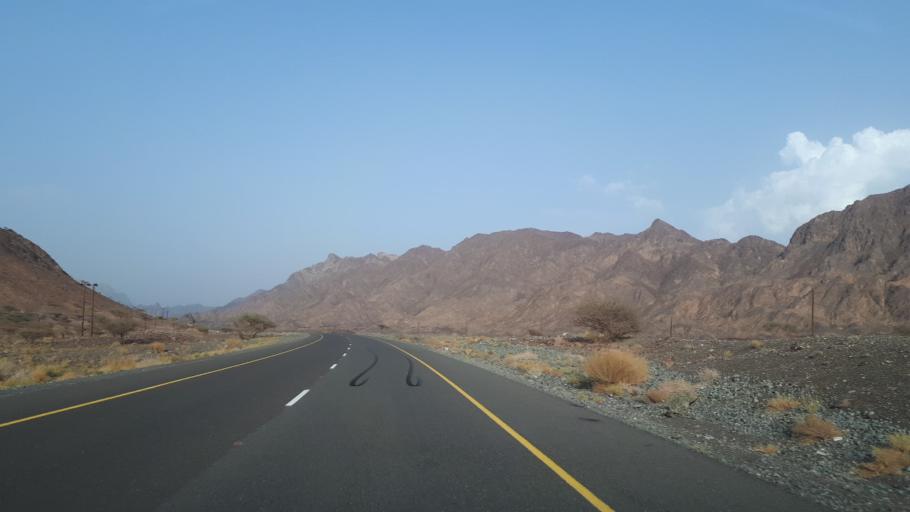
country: OM
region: Az Zahirah
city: Yanqul
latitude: 23.4919
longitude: 56.8684
